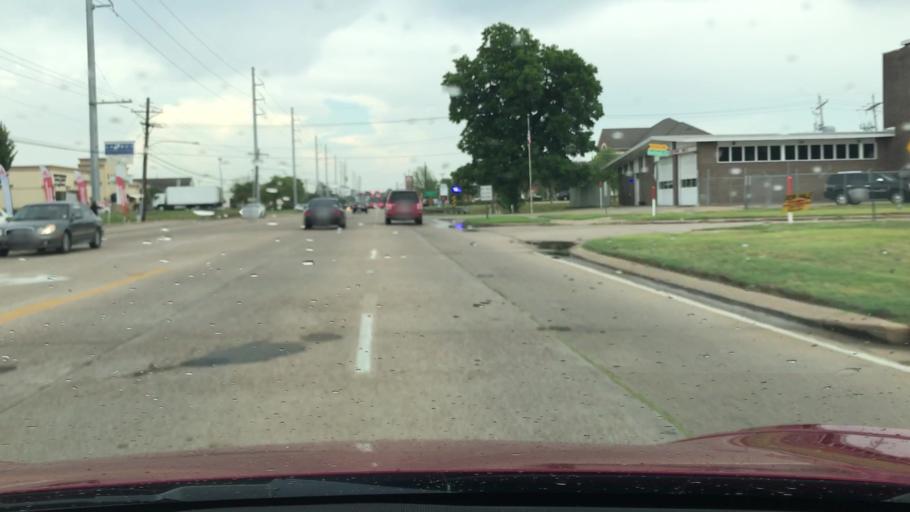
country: US
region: Louisiana
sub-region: Bossier Parish
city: Bossier City
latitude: 32.4434
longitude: -93.7255
